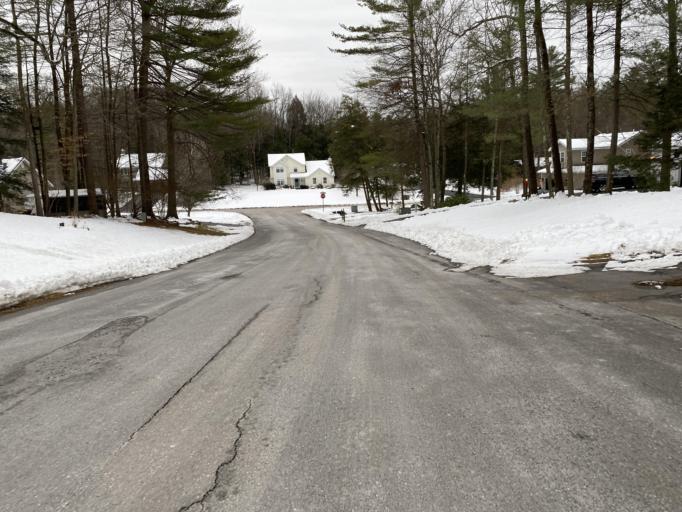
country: US
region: New York
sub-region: Saratoga County
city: Milton
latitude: 43.0954
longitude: -73.9067
